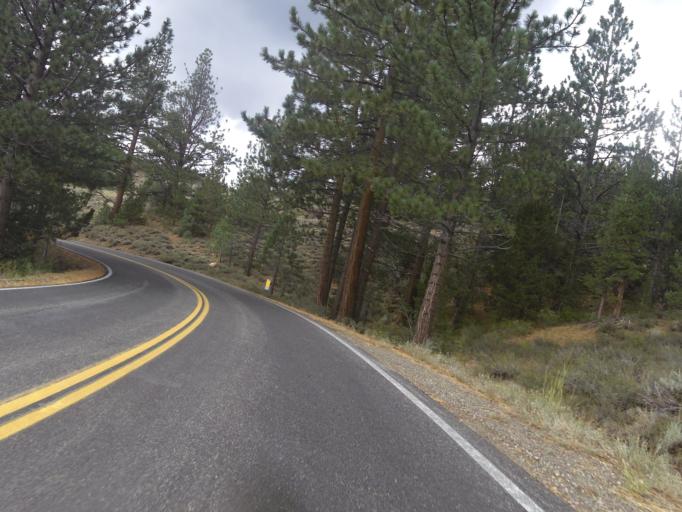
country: US
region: Nevada
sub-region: Douglas County
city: Gardnerville Ranchos
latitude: 38.6722
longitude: -119.6637
